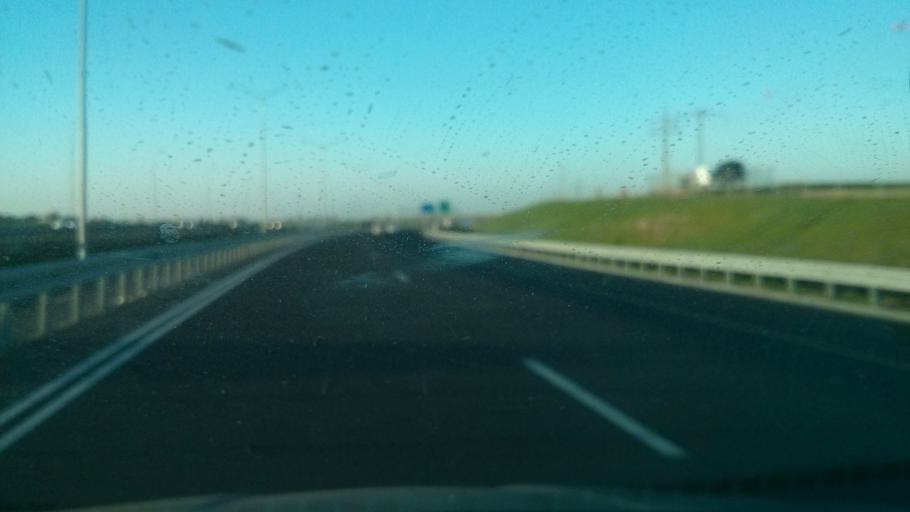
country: IL
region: Southern District
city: Lehavim
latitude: 31.4369
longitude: 34.7731
